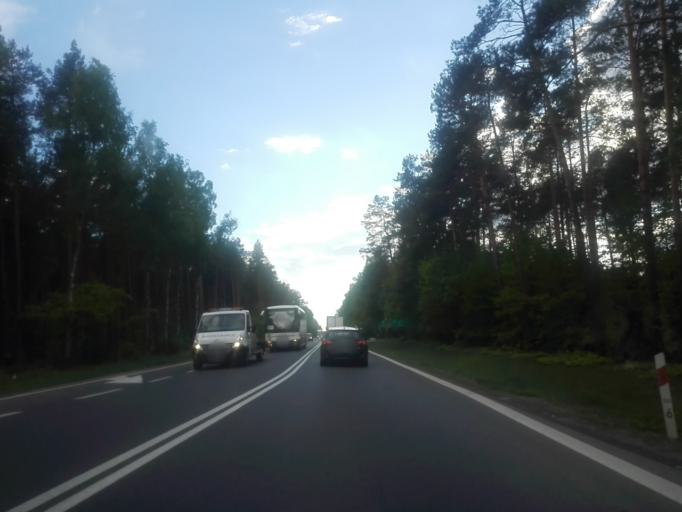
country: PL
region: Masovian Voivodeship
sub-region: Powiat wyszkowski
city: Dlugosiodlo
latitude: 52.6932
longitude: 21.6509
